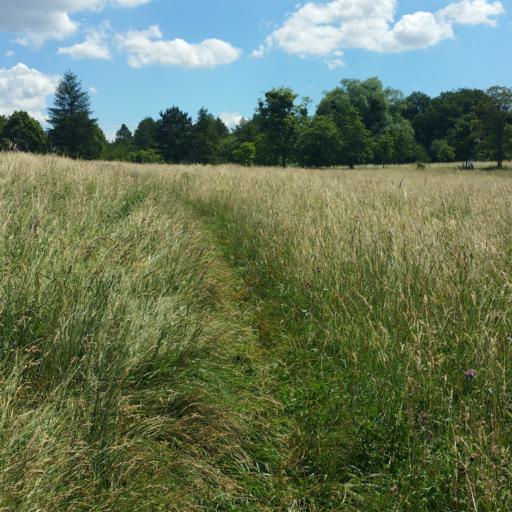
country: AT
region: Lower Austria
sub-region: Politischer Bezirk Modling
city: Perchtoldsdorf
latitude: 48.2124
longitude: 16.2745
